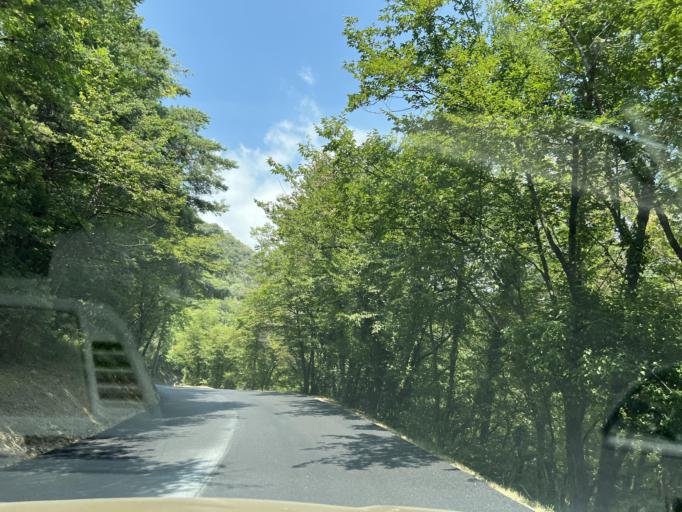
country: FR
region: Provence-Alpes-Cote d'Azur
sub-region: Departement des Alpes-Maritimes
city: Tourrettes-sur-Loup
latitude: 43.7549
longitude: 6.9910
